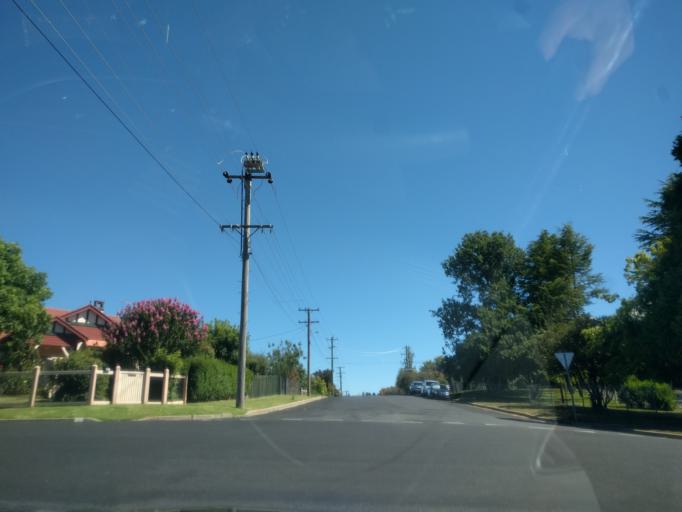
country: AU
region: New South Wales
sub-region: Armidale Dumaresq
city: Armidale
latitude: -30.5226
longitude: 151.6639
